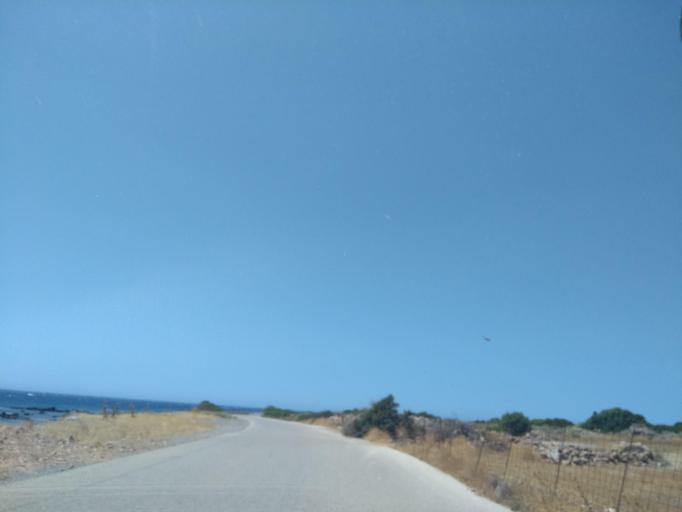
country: GR
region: Crete
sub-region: Nomos Chanias
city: Vryses
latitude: 35.3533
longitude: 23.5353
